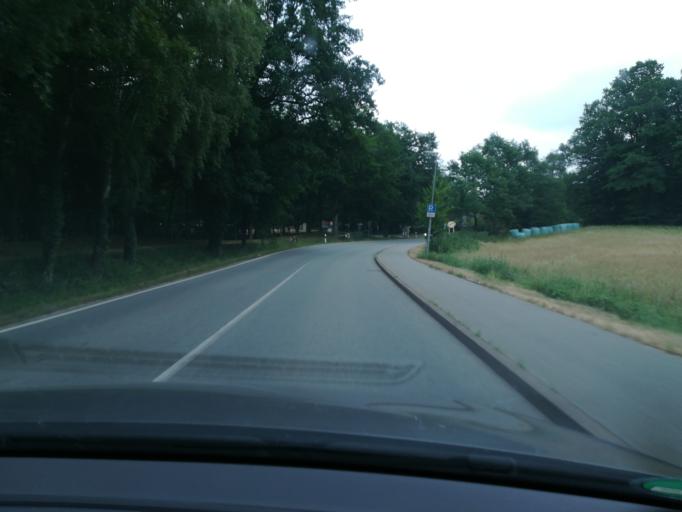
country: DE
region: Schleswig-Holstein
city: Grossensee
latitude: 53.6119
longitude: 10.3478
